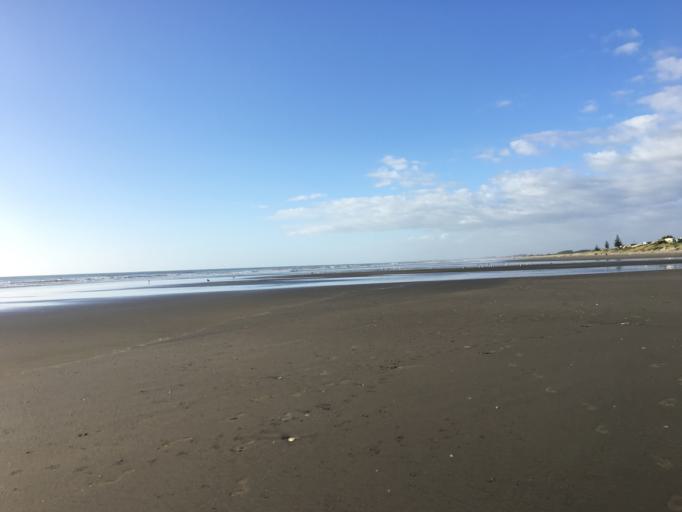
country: NZ
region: Wellington
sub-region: Kapiti Coast District
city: Paraparaumu
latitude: -40.8578
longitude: 175.0268
